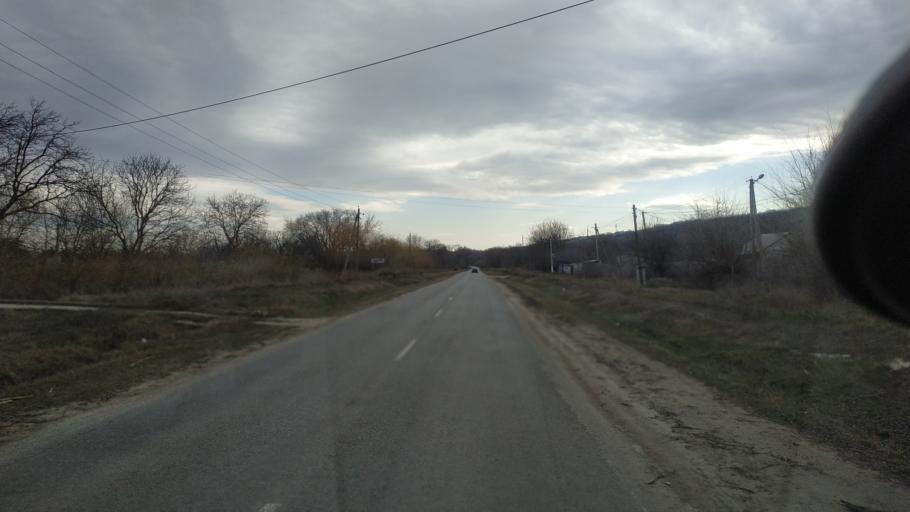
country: MD
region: Chisinau
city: Vadul lui Voda
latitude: 47.1361
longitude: 29.0613
